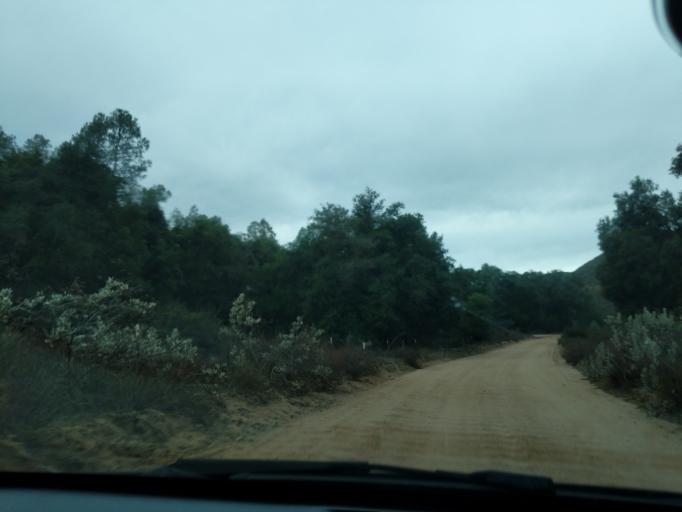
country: US
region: California
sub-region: Monterey County
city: Soledad
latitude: 36.5648
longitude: -121.2204
